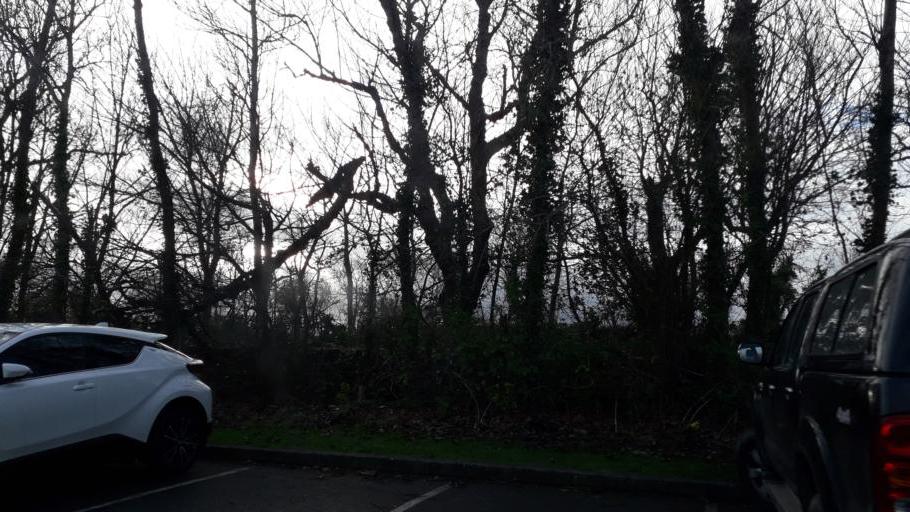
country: IE
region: Leinster
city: Balrothery
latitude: 53.5815
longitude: -6.1604
